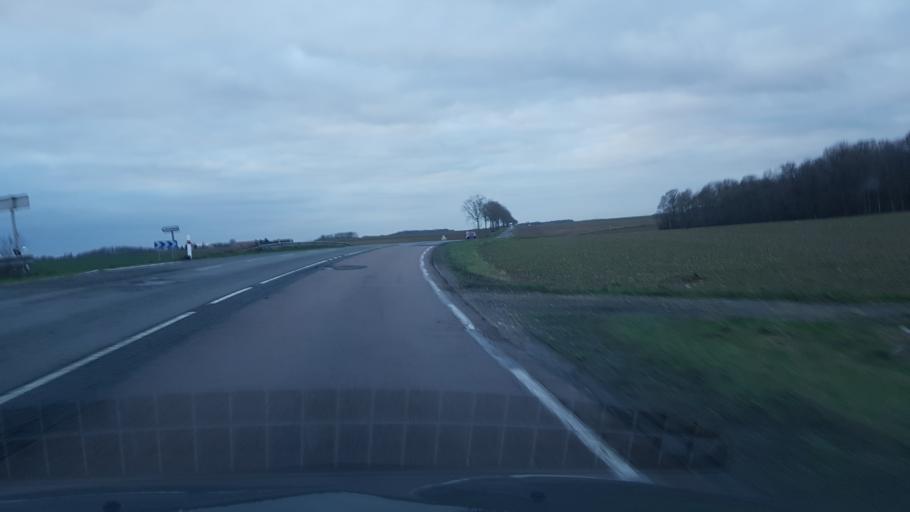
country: FR
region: Ile-de-France
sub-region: Departement de Seine-et-Marne
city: Choisy-en-Brie
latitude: 48.6924
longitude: 3.2204
